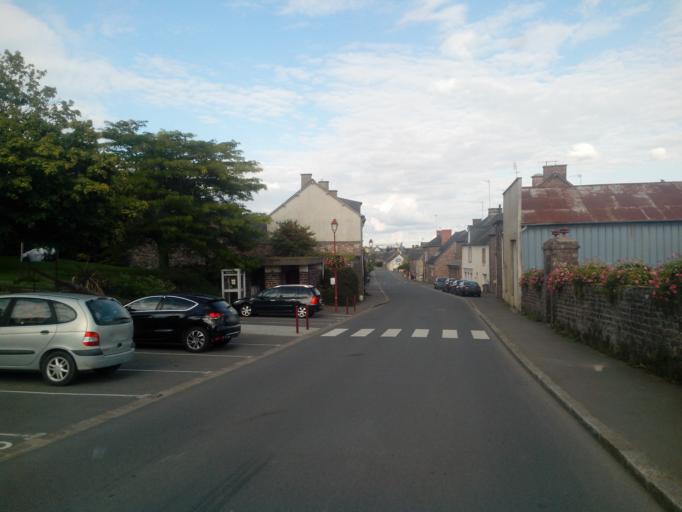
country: FR
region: Brittany
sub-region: Departement d'Ille-et-Vilaine
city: Iffendic
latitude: 48.1288
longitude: -2.0337
